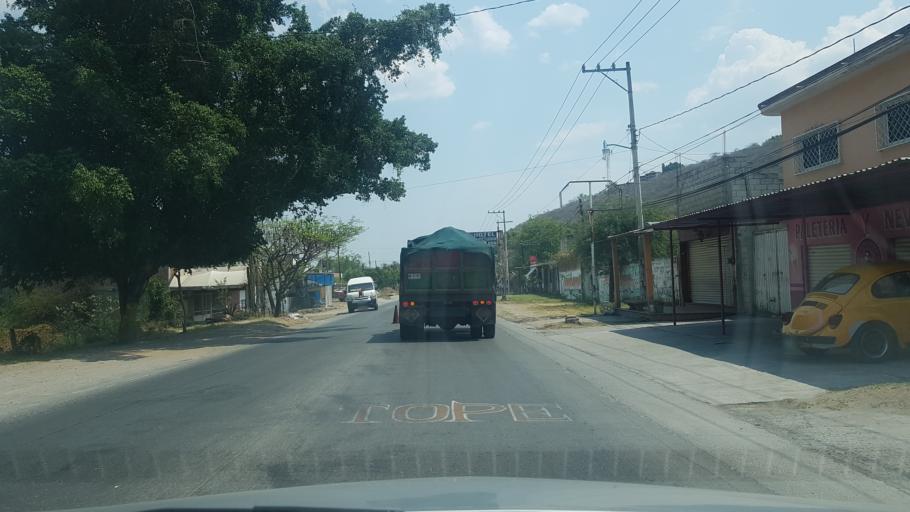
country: MX
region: Morelos
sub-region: Tlaltizapan de Zapata
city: Colonia Palo Prieto (Chipitongo)
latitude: 18.7154
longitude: -99.1190
